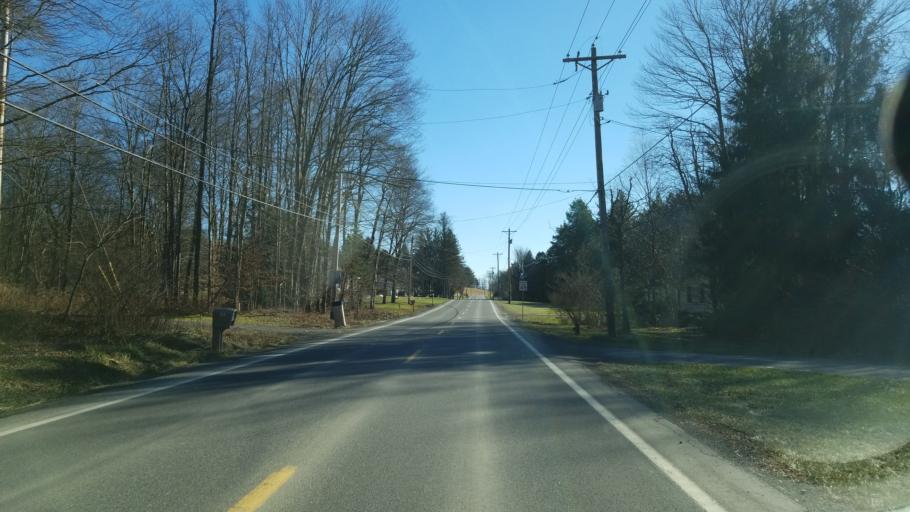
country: US
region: Pennsylvania
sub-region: Jefferson County
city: Falls Creek
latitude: 41.1665
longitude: -78.8290
